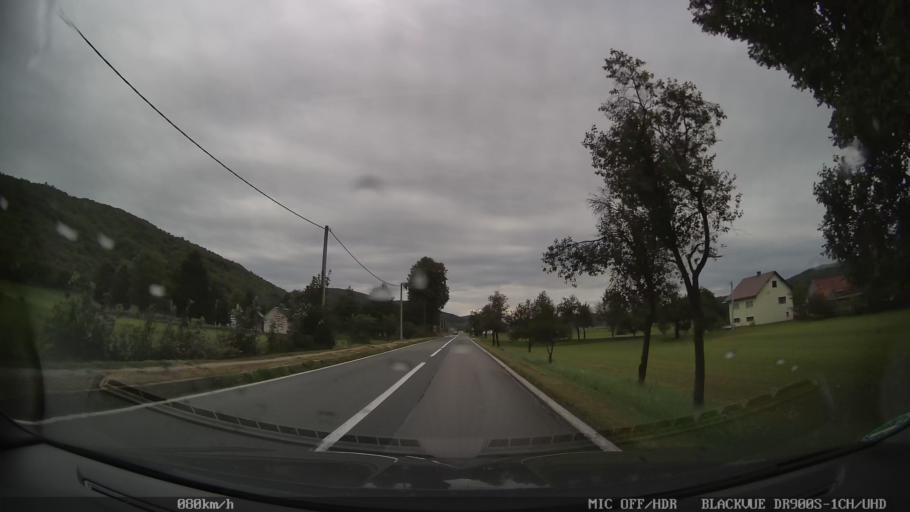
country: HR
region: Licko-Senjska
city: Brinje
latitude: 44.9160
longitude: 15.1562
